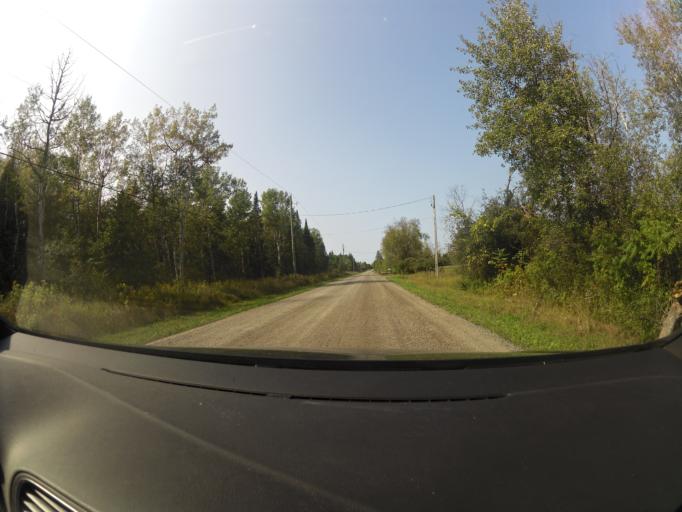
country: CA
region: Ontario
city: Carleton Place
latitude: 45.3158
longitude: -76.1396
